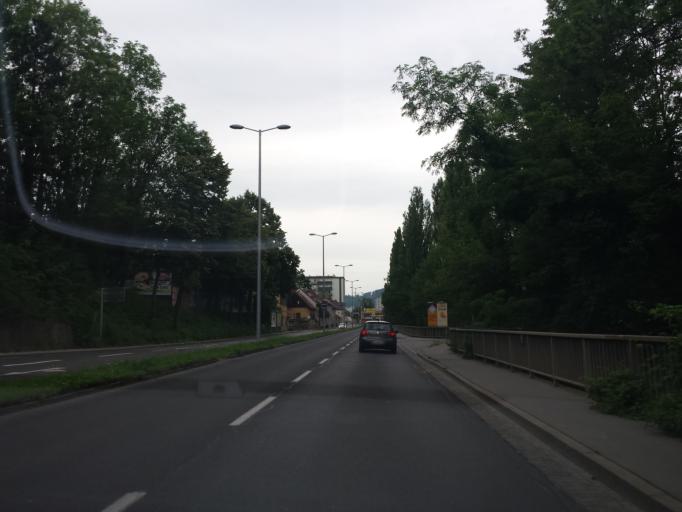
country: AT
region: Styria
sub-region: Graz Stadt
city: Goesting
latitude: 47.0844
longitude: 15.4147
